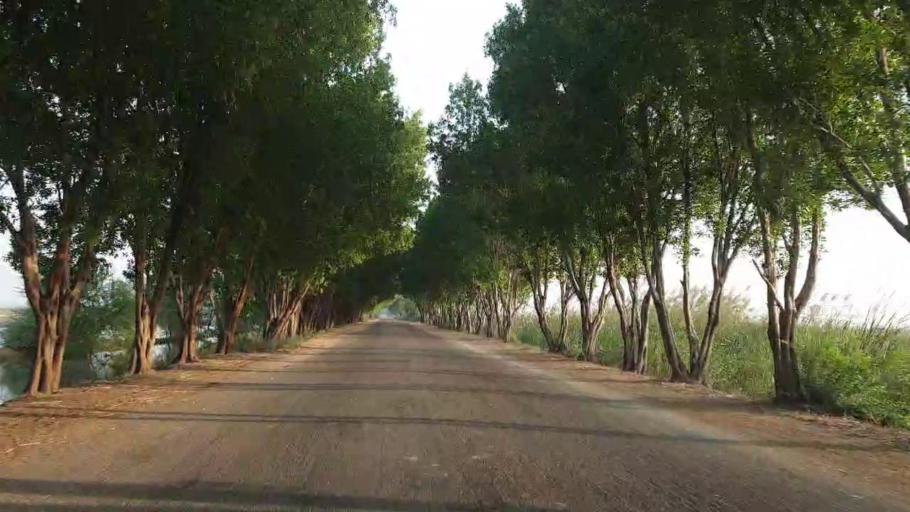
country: PK
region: Sindh
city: Tando Bago
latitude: 24.7273
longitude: 68.9430
